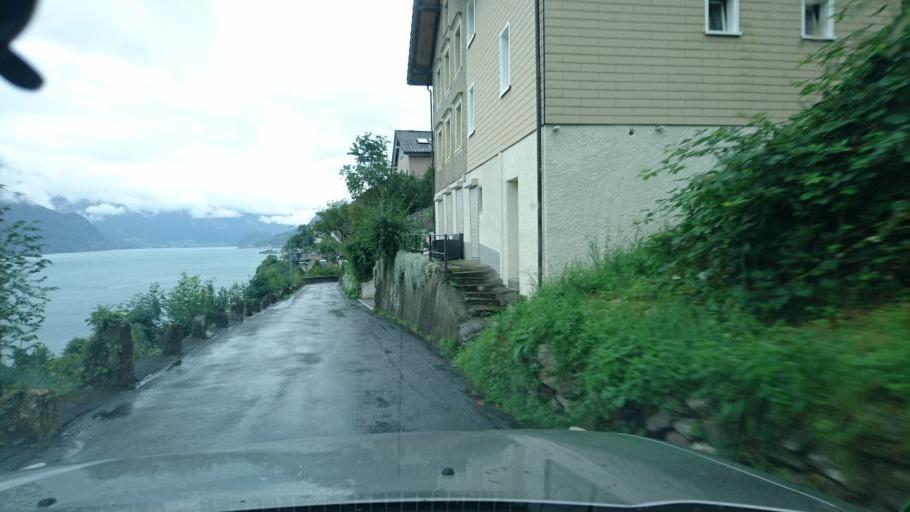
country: CH
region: Saint Gallen
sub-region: Wahlkreis See-Gaster
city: Amden
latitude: 47.1167
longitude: 9.1706
